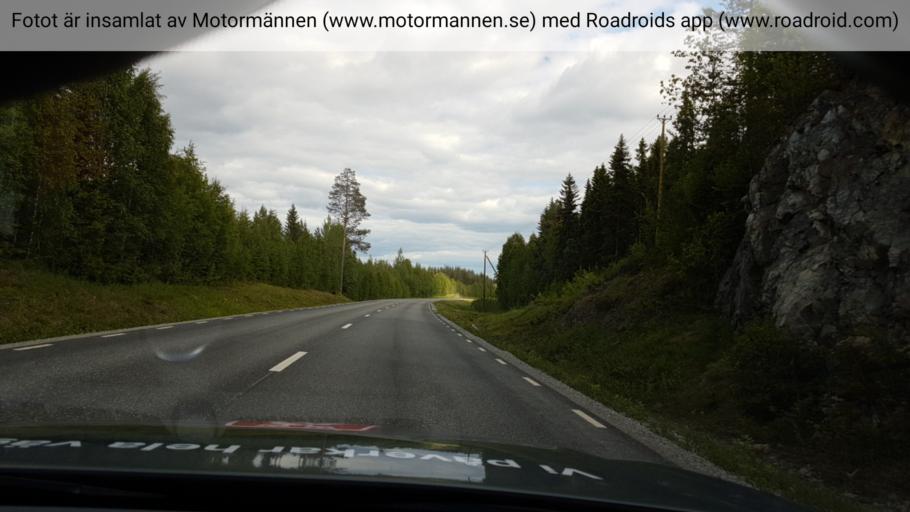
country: SE
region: Jaemtland
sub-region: Stroemsunds Kommun
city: Stroemsund
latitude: 64.1967
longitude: 15.6186
